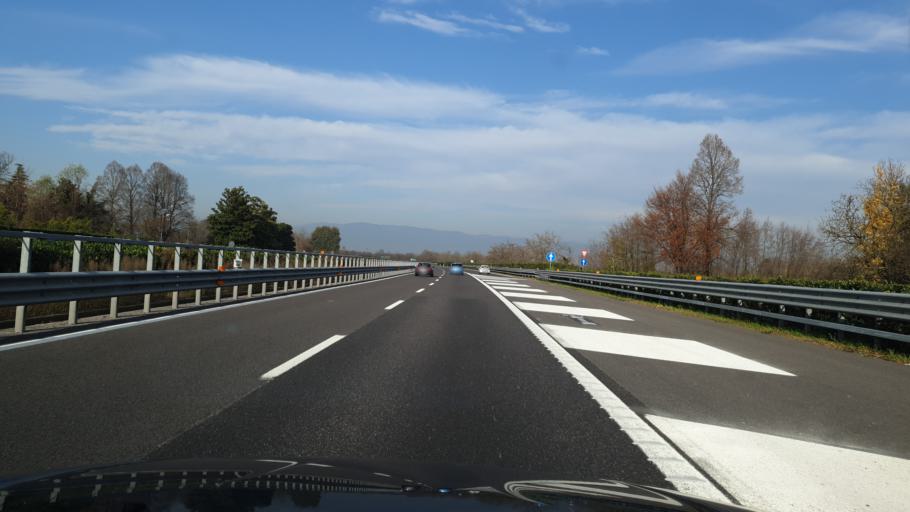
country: IT
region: Veneto
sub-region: Provincia di Vicenza
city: Lisiera
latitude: 45.5634
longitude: 11.6141
